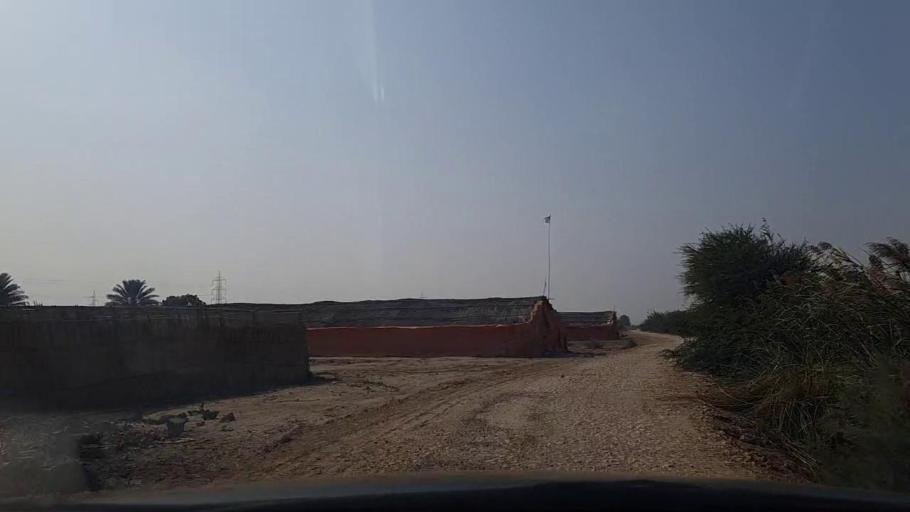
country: PK
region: Sindh
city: Mirpur Sakro
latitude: 24.5704
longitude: 67.7782
